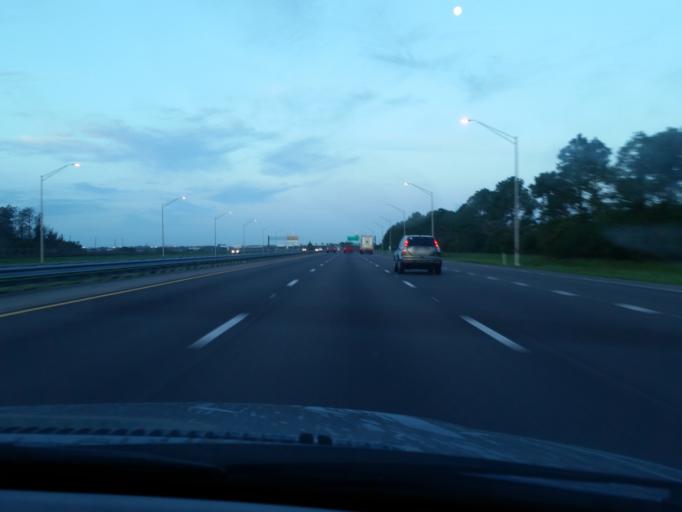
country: US
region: Florida
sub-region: Orange County
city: Conway
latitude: 28.4486
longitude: -81.2709
